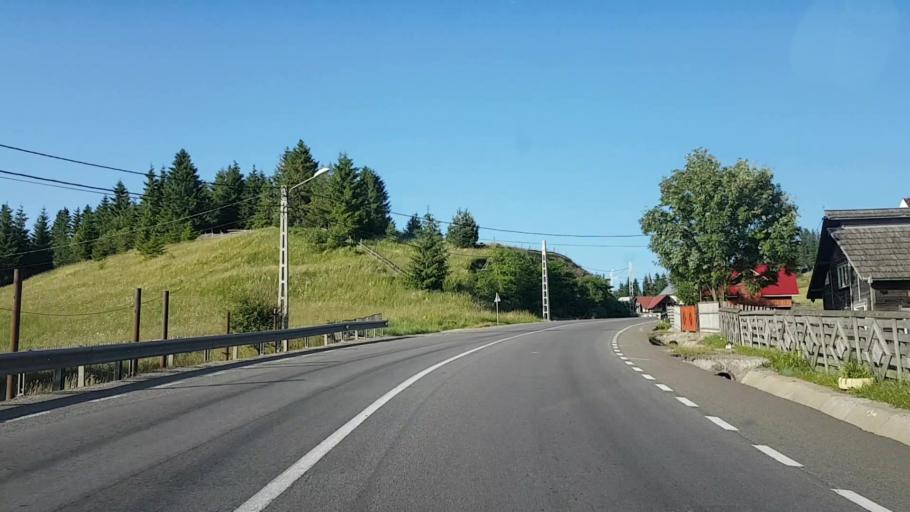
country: RO
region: Bistrita-Nasaud
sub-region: Comuna Lunca Ilvei
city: Lunca Ilvei
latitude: 47.2347
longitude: 24.9987
